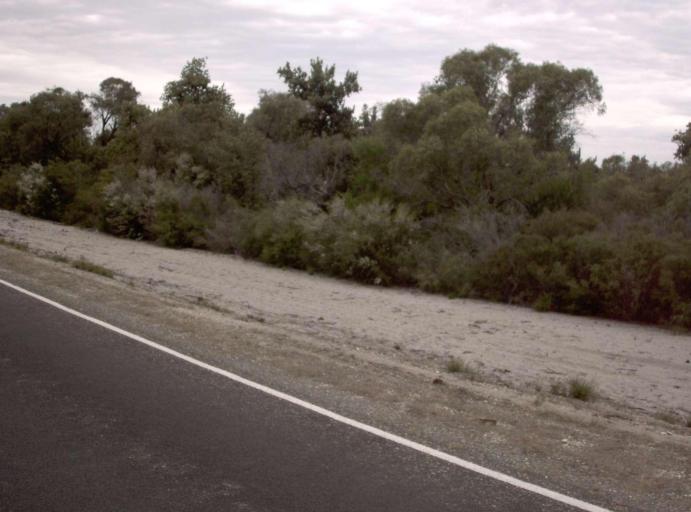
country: AU
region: Victoria
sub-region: Wellington
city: Sale
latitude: -38.1805
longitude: 147.3776
